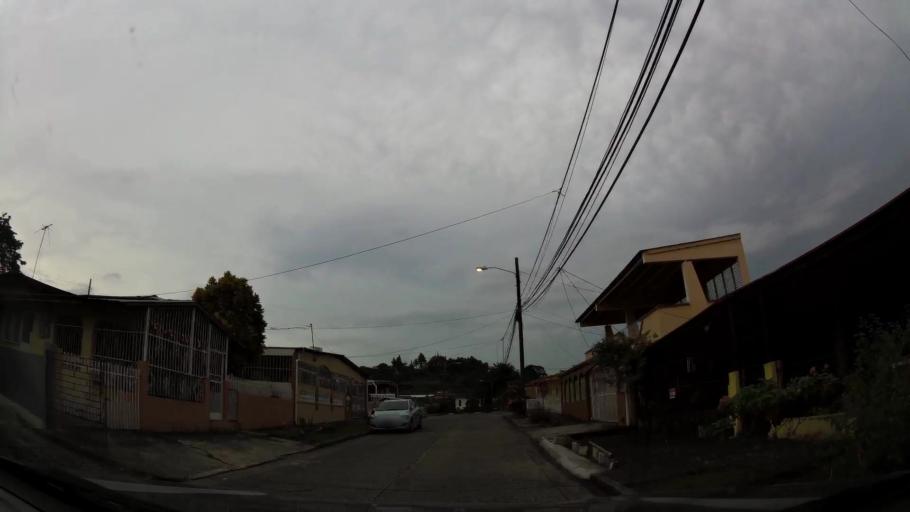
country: PA
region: Panama
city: Panama
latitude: 9.0204
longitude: -79.5248
